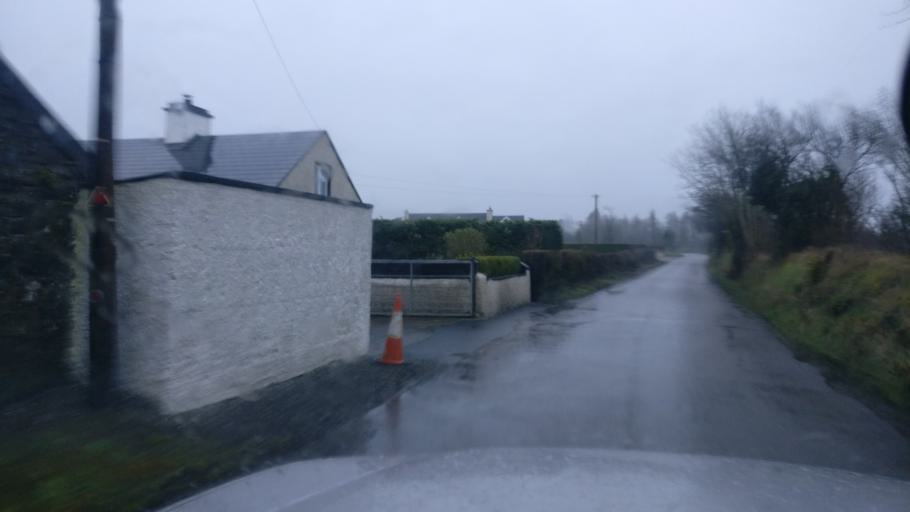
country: IE
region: Connaught
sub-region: County Galway
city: Ballinasloe
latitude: 53.3141
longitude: -8.3674
